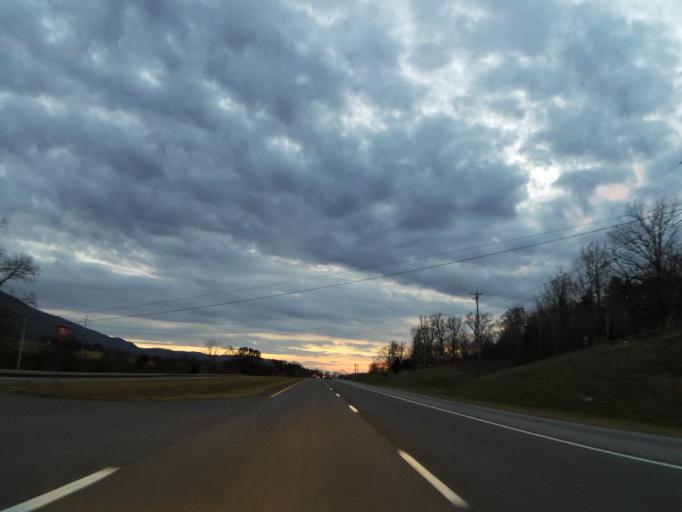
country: US
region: Tennessee
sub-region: McMinn County
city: Etowah
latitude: 35.2386
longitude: -84.5650
